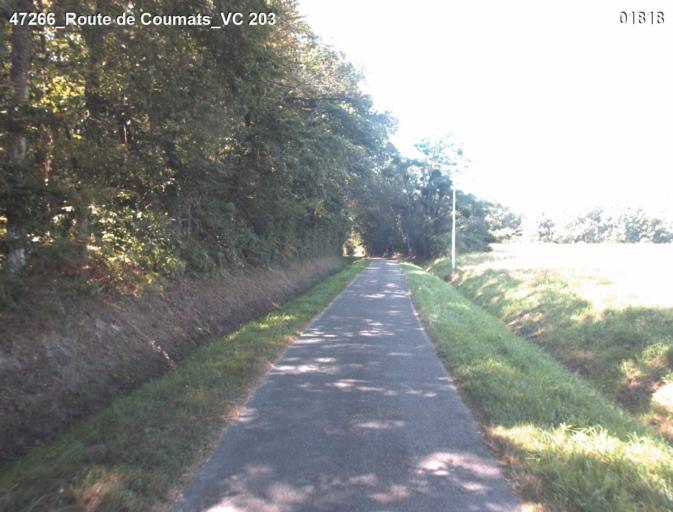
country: FR
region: Aquitaine
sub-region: Departement des Landes
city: Gabarret
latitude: 44.0039
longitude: 0.0976
